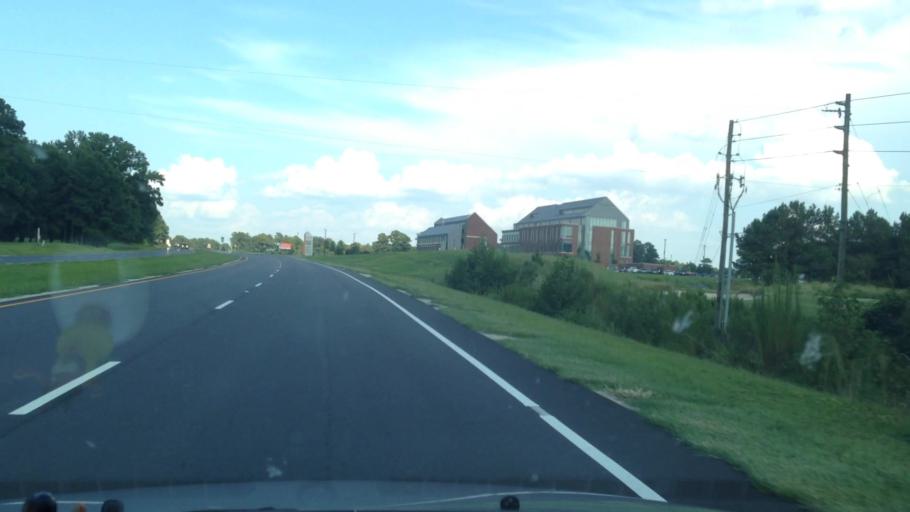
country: US
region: North Carolina
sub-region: Harnett County
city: Buies Creek
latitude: 35.4069
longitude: -78.7611
